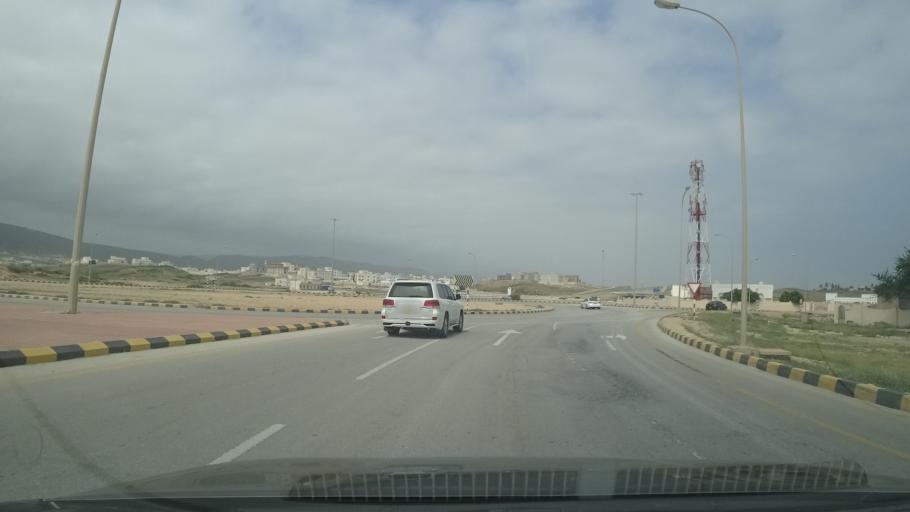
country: OM
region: Zufar
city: Salalah
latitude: 17.0502
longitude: 54.3871
